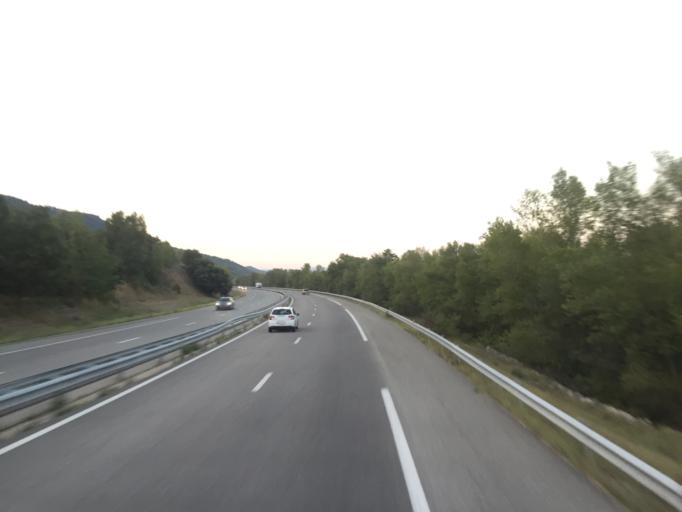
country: FR
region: Provence-Alpes-Cote d'Azur
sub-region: Departement des Alpes-de-Haute-Provence
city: Oraison
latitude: 43.9746
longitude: 5.9091
